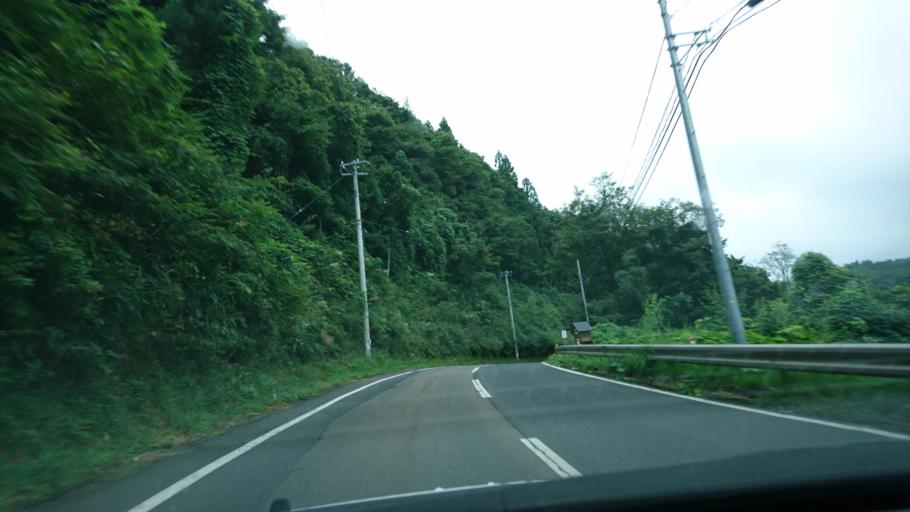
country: JP
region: Iwate
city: Ichinoseki
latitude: 38.9114
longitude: 141.0655
